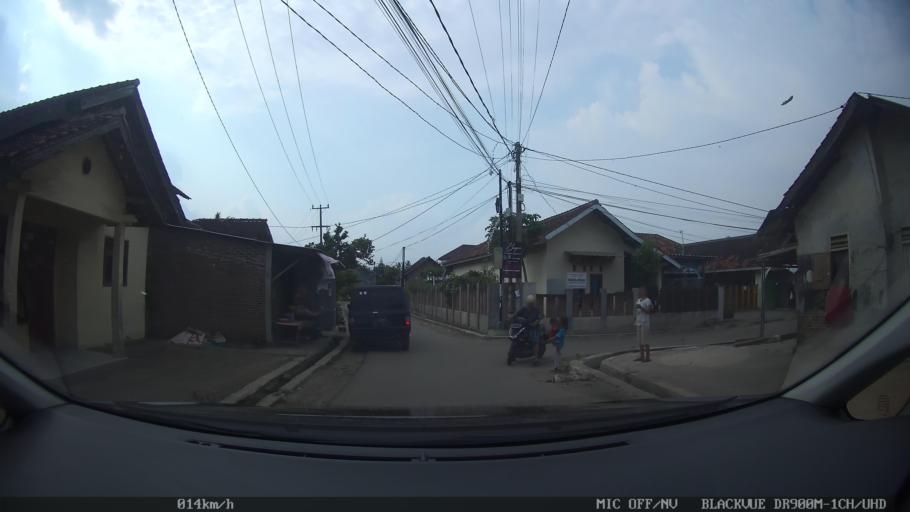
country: ID
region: Lampung
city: Kedaton
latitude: -5.3715
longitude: 105.2180
